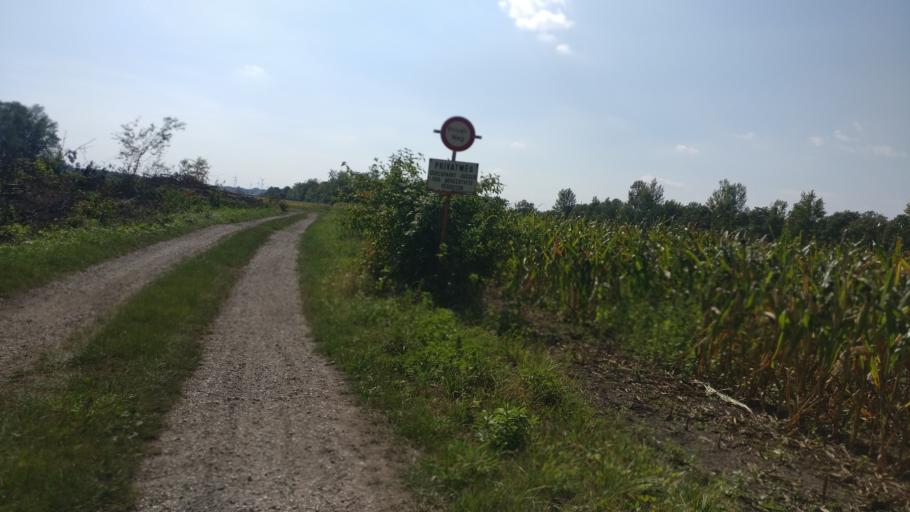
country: AT
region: Lower Austria
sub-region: Politischer Bezirk Wien-Umgebung
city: Moosbrunn
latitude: 47.9949
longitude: 16.4117
